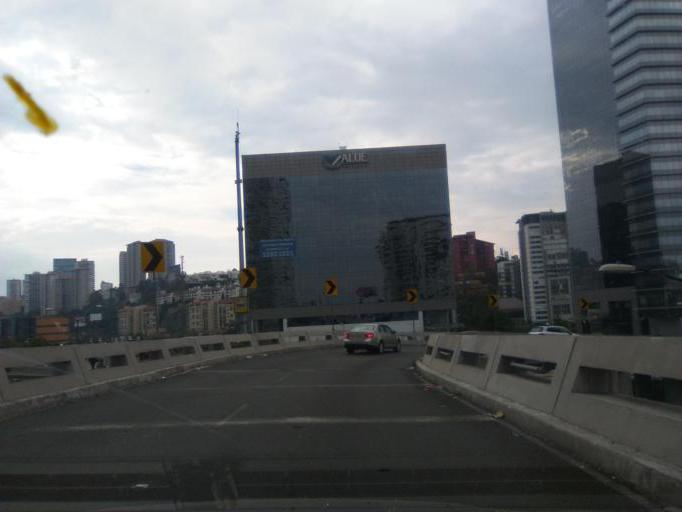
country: MX
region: Mexico City
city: Col. Bosques de las Lomas
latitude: 19.3633
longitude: -99.2662
